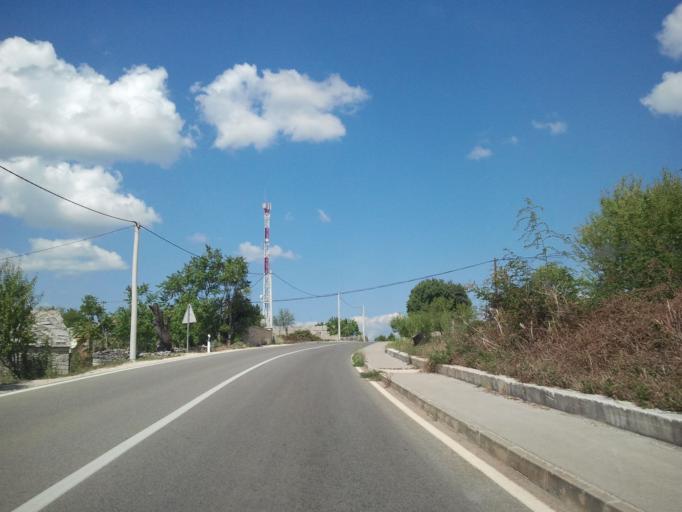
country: HR
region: Zadarska
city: Benkovac
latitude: 44.0417
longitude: 15.6174
